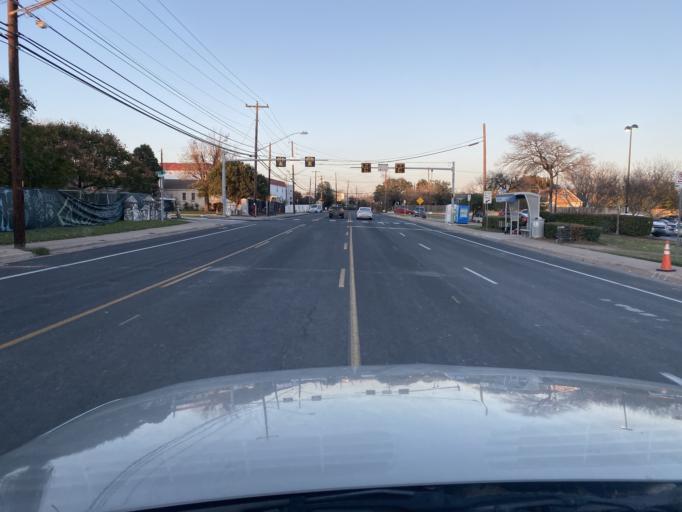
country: US
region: Texas
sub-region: Travis County
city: Austin
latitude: 30.3011
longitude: -97.7217
